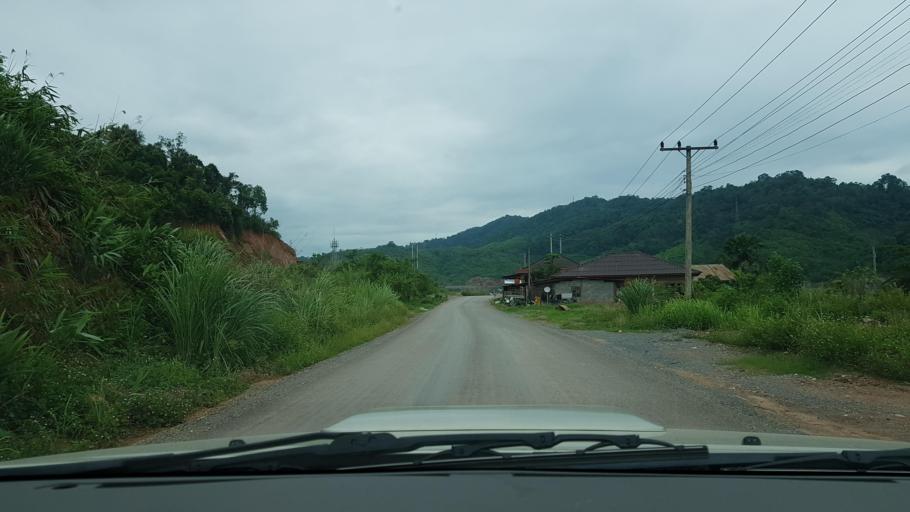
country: LA
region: Oudomxai
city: Muang Xay
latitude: 20.6581
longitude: 101.9819
